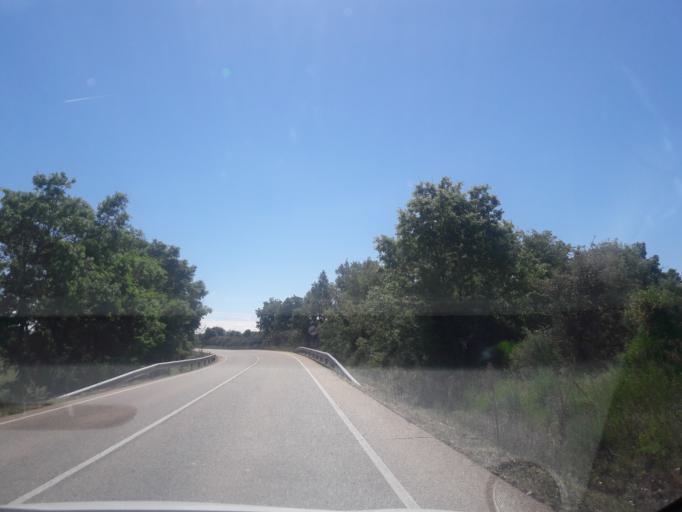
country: ES
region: Castille and Leon
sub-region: Provincia de Salamanca
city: Encinasola de los Comendadores
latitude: 40.9941
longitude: -6.5466
